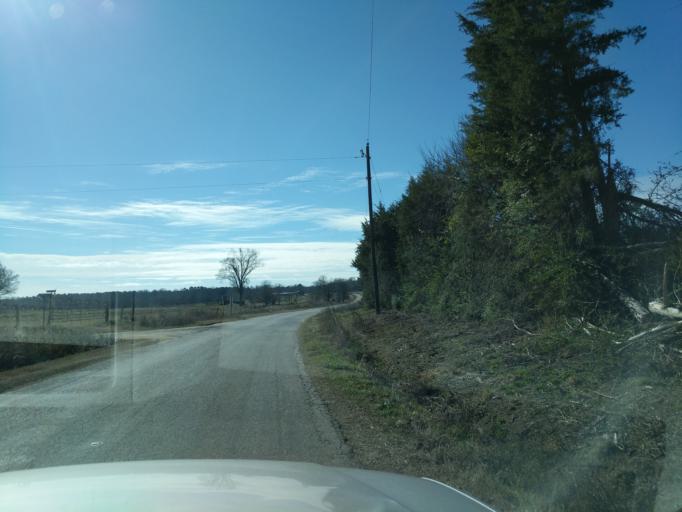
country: US
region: South Carolina
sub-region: Saluda County
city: Saluda
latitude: 34.0142
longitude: -81.8469
